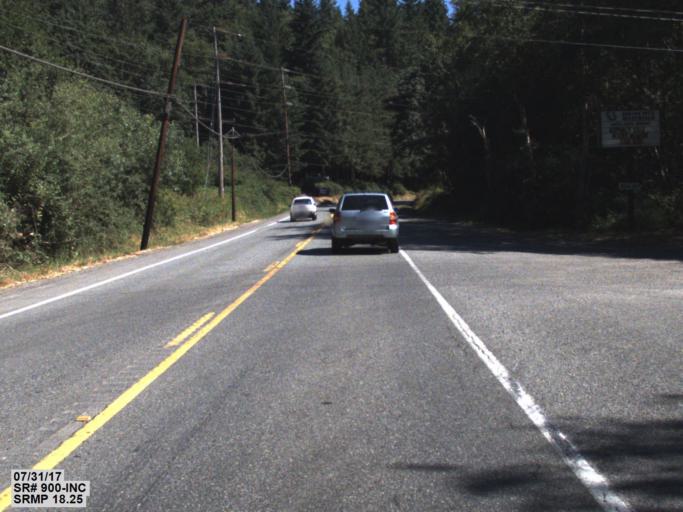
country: US
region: Washington
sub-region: King County
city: East Renton Highlands
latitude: 47.5086
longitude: -122.0882
